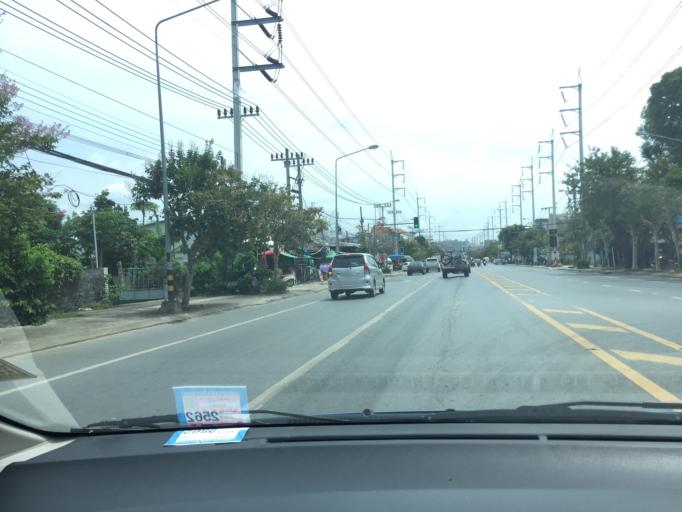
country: TH
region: Phuket
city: Mueang Phuket
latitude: 7.8580
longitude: 98.3804
